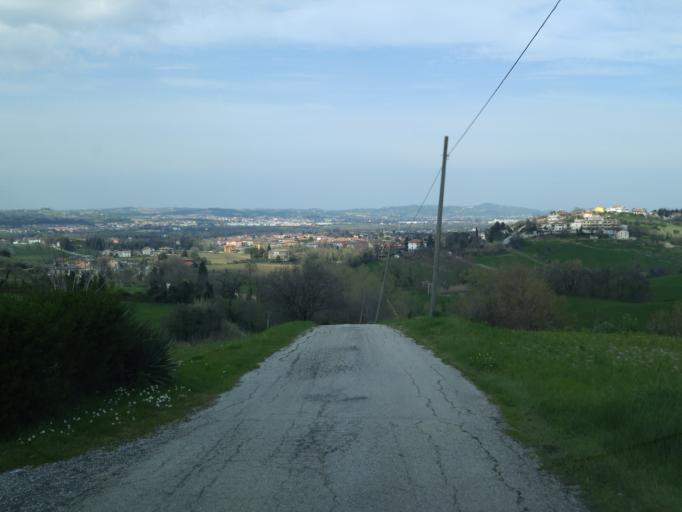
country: IT
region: The Marches
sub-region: Provincia di Pesaro e Urbino
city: Villanova
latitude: 43.7283
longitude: 12.9343
